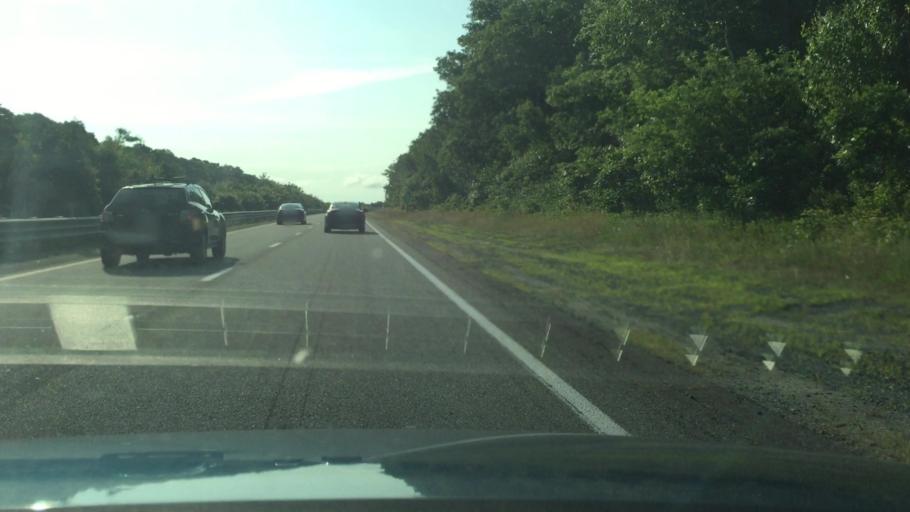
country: US
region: Massachusetts
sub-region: Barnstable County
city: East Sandwich
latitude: 41.7375
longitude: -70.4772
